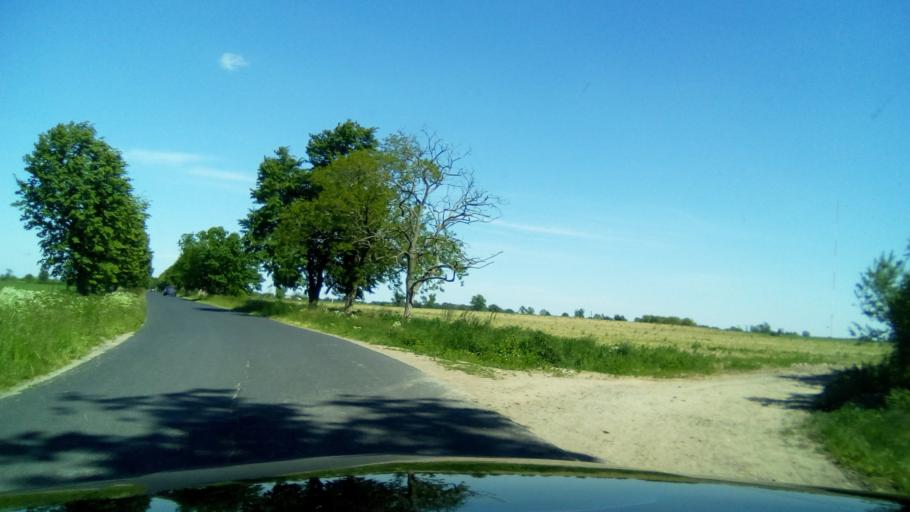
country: PL
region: Greater Poland Voivodeship
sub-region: Powiat gnieznienski
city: Niechanowo
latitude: 52.4557
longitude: 17.6325
